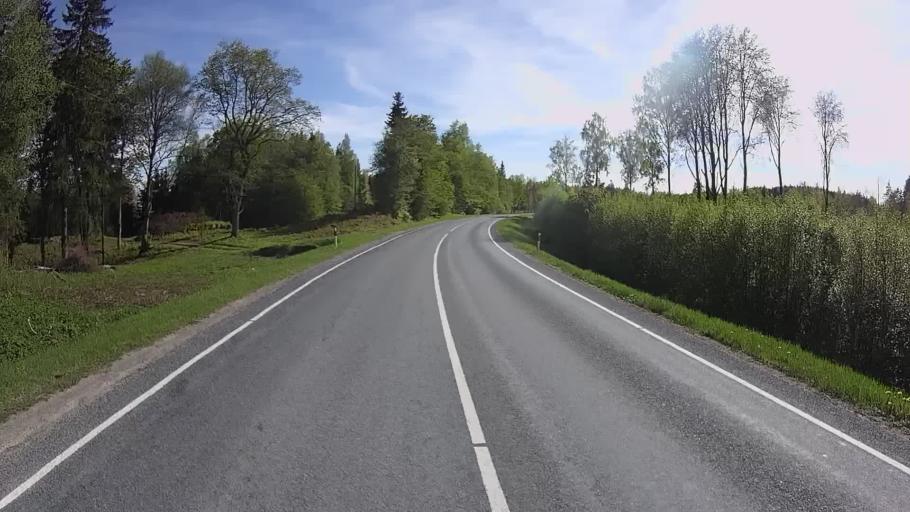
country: EE
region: Vorumaa
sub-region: Antsla vald
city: Vana-Antsla
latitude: 57.9728
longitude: 26.4646
